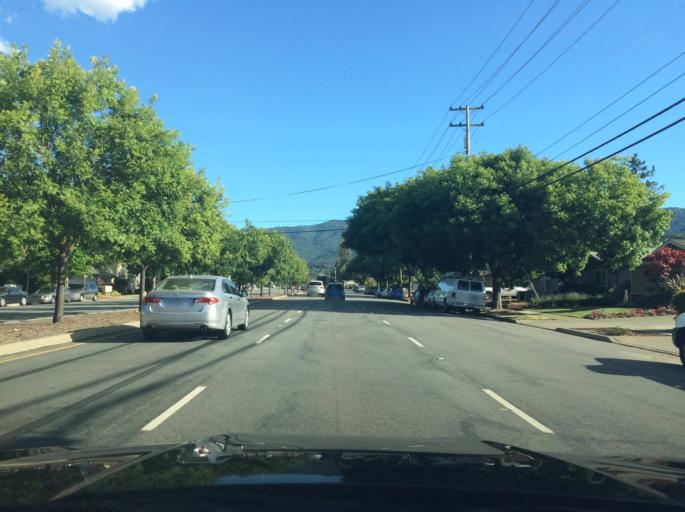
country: US
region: California
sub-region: Santa Clara County
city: Cambrian Park
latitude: 37.2385
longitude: -121.9036
